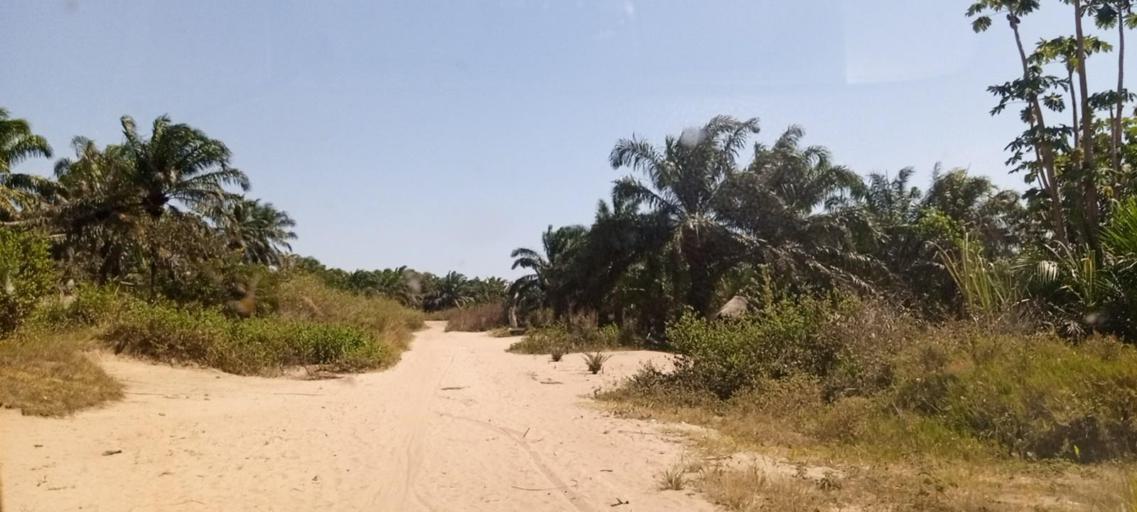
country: CD
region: Kasai-Oriental
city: Kabinda
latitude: -5.9638
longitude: 24.7700
